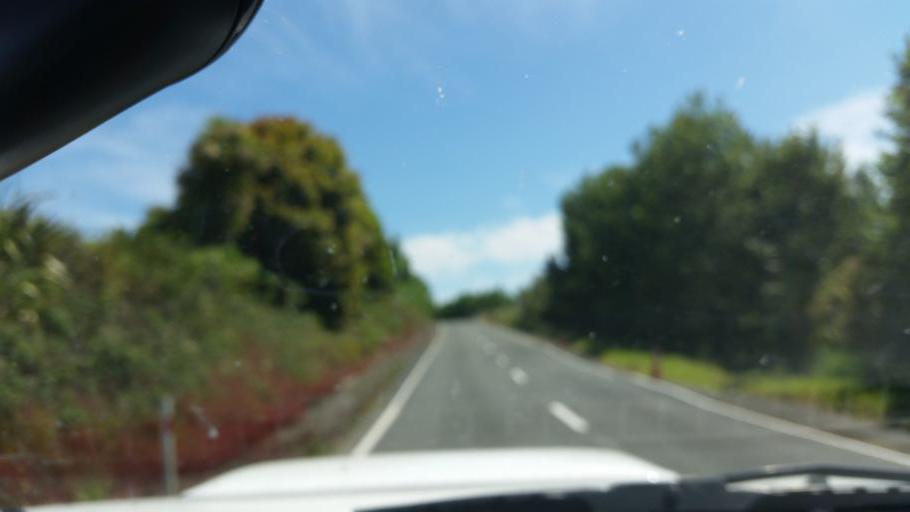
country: NZ
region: Auckland
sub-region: Auckland
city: Wellsford
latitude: -36.2136
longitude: 174.3906
